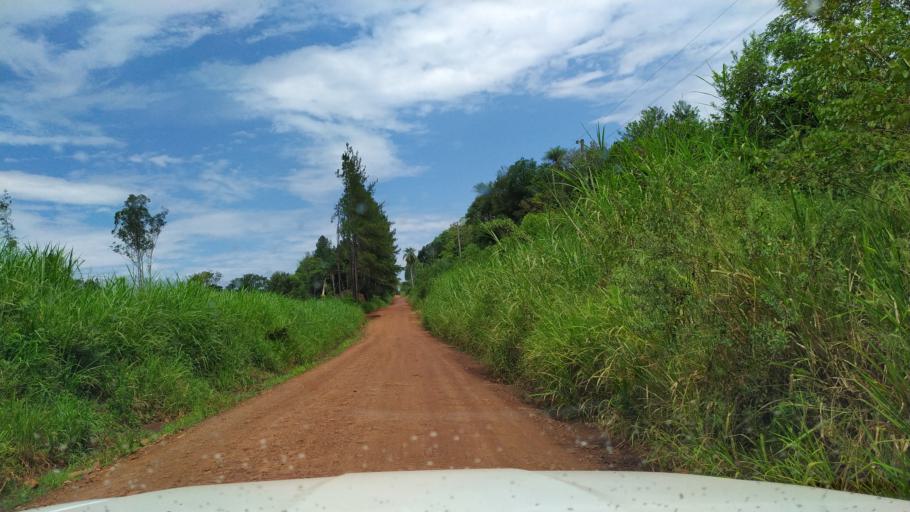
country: AR
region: Misiones
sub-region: Departamento de Eldorado
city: Eldorado
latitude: -26.4425
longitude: -54.6041
